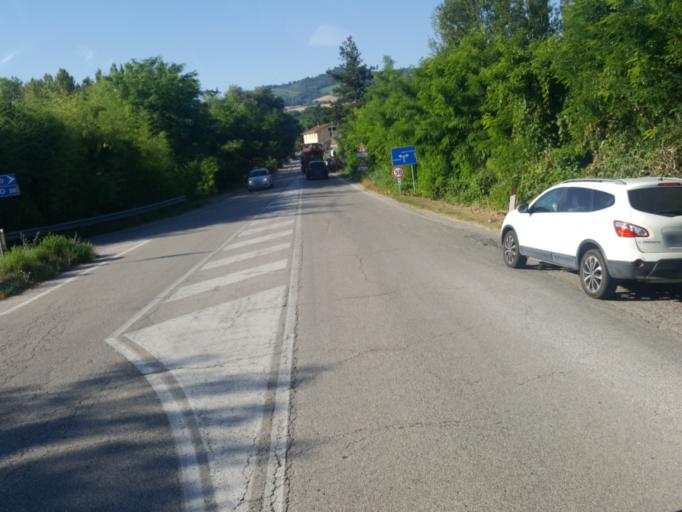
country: IT
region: The Marches
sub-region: Provincia di Pesaro e Urbino
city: Montecalvo in Foglia
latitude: 43.7955
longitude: 12.6187
